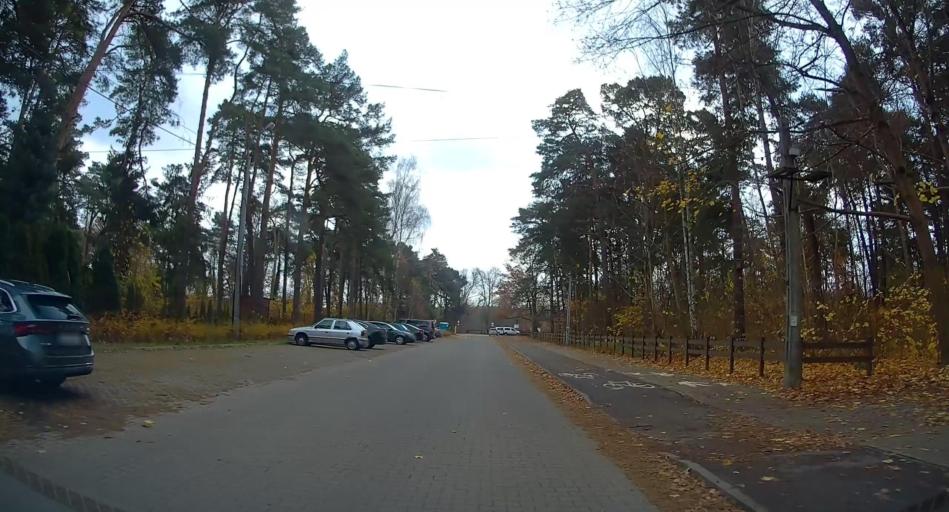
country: PL
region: Masovian Voivodeship
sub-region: Powiat piaseczynski
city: Zabieniec
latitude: 52.0527
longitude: 21.0233
